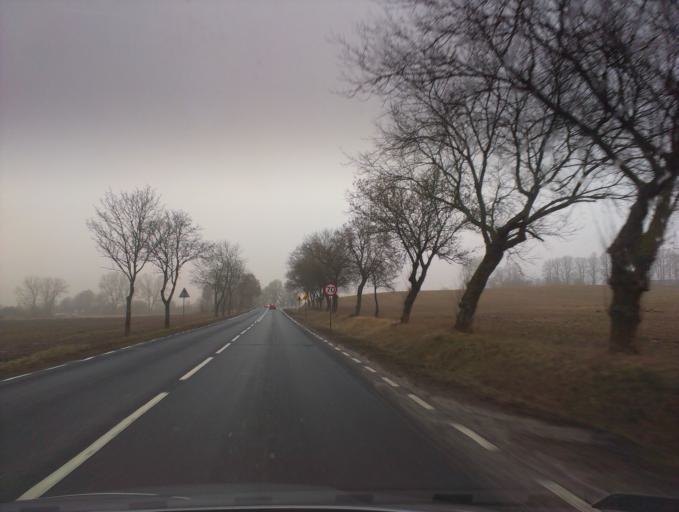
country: PL
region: West Pomeranian Voivodeship
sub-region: Powiat szczecinecki
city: Szczecinek
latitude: 53.7303
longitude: 16.6719
